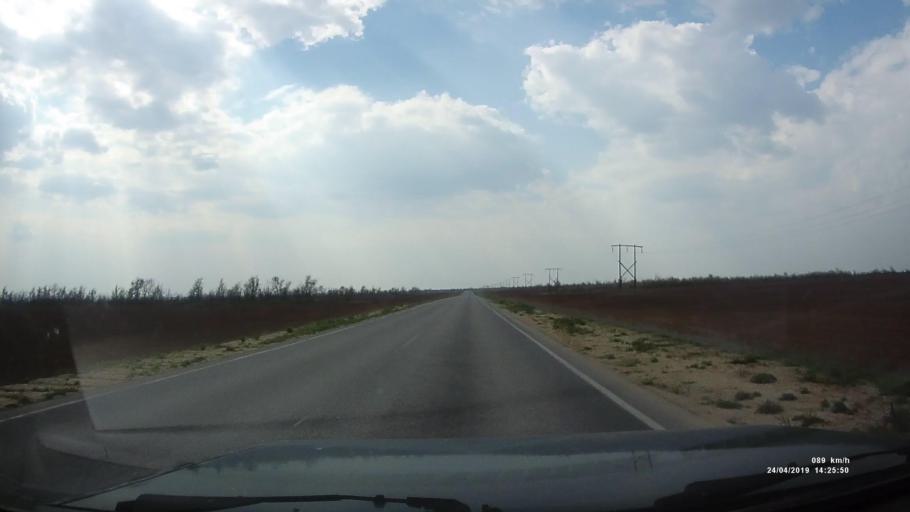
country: RU
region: Kalmykiya
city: Arshan'
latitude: 46.3320
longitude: 44.0747
